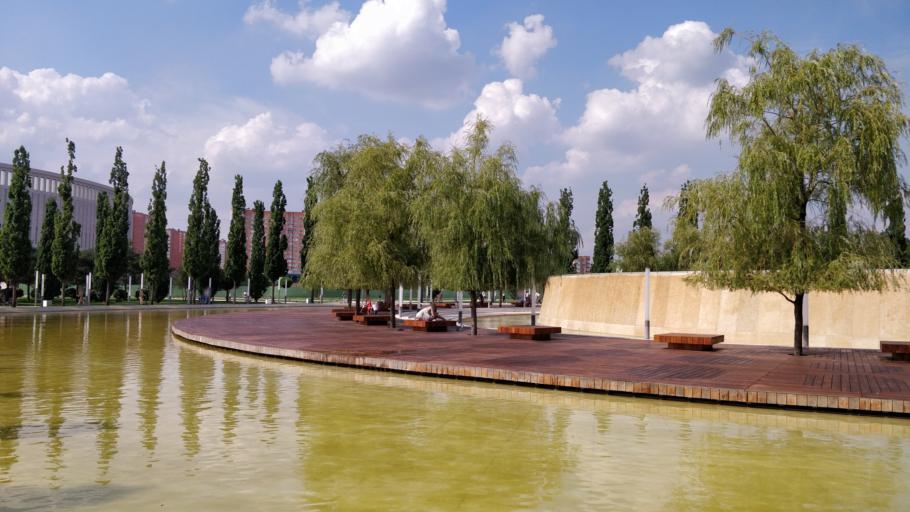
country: RU
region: Krasnodarskiy
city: Krasnodar
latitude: 45.0414
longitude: 39.0315
